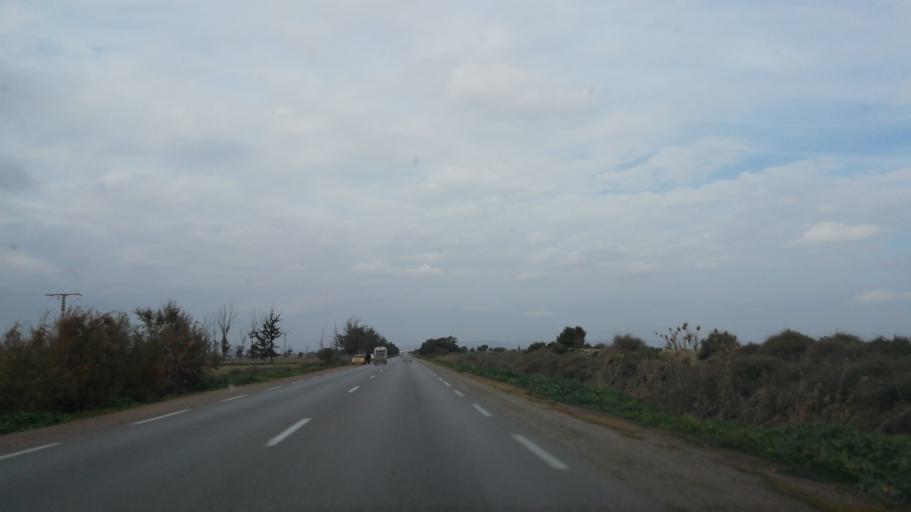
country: DZ
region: Mostaganem
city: Mostaganem
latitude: 35.6739
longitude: 0.0575
